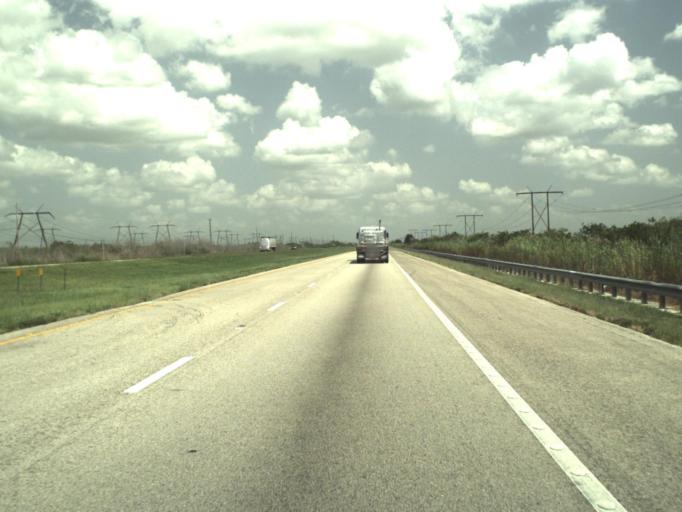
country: US
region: Florida
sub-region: Broward County
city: Weston
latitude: 26.1513
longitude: -80.4432
